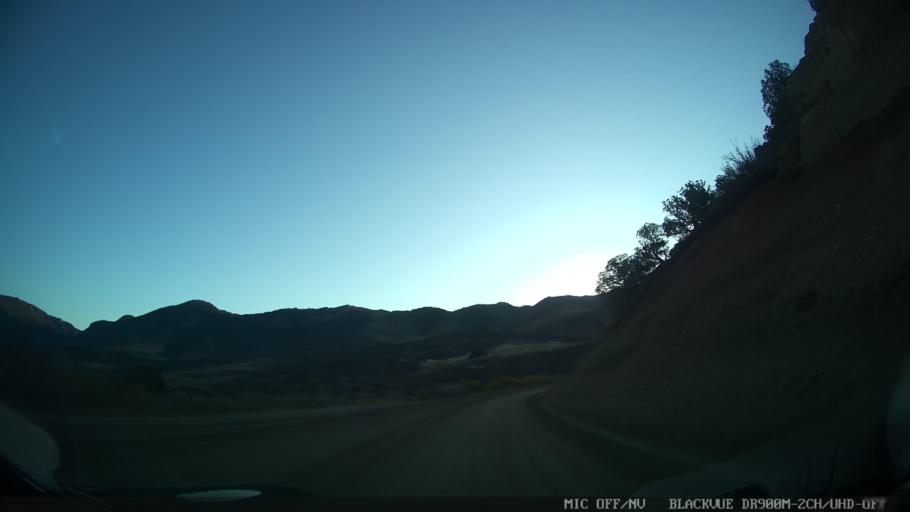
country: US
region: Colorado
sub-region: Grand County
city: Kremmling
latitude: 39.9661
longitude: -106.5109
